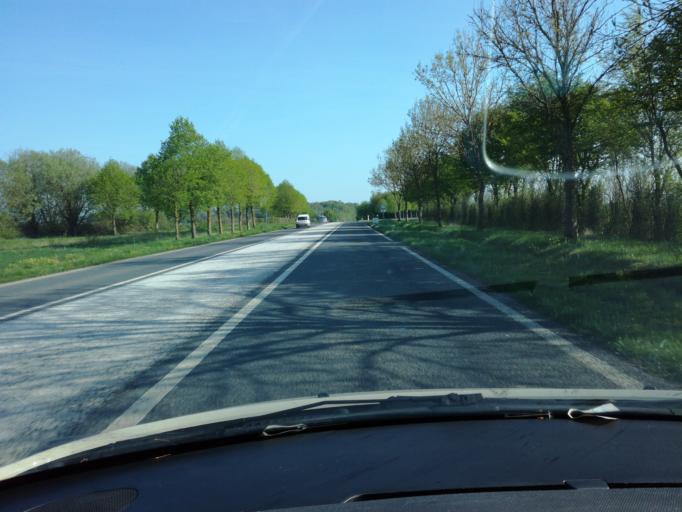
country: FR
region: Picardie
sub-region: Departement de la Somme
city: Poix-de-Picardie
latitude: 49.7966
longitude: 1.9753
